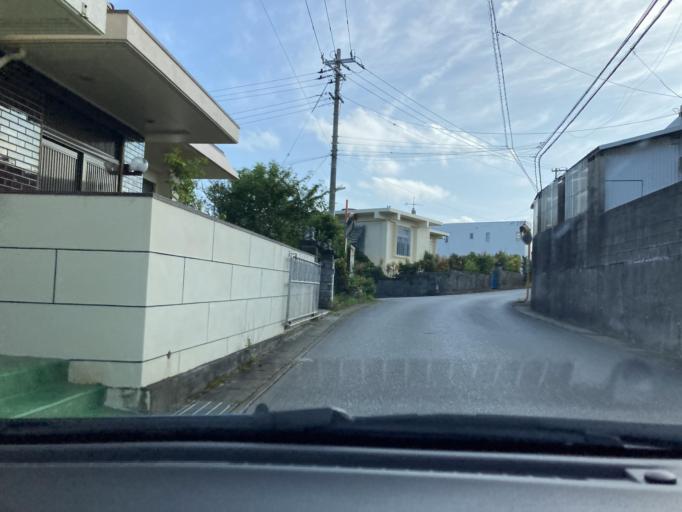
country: JP
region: Okinawa
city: Ginowan
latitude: 26.2326
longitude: 127.7419
